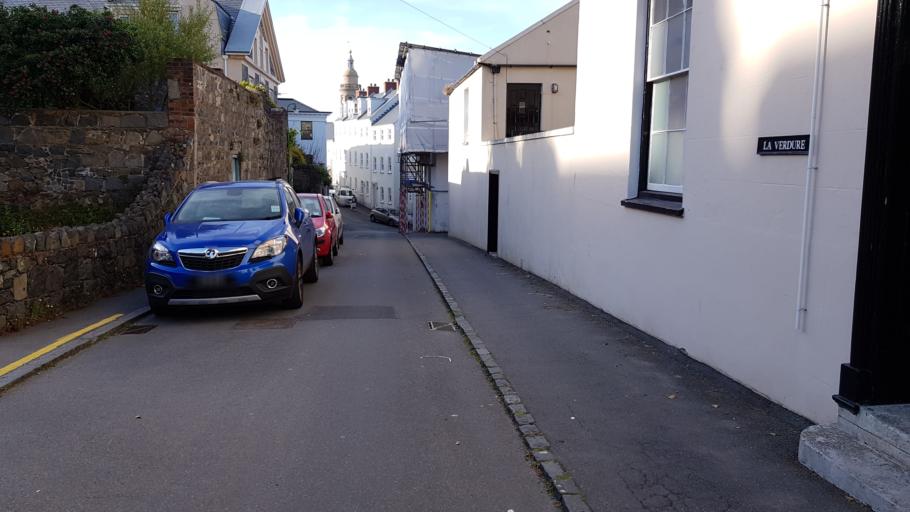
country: GG
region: St Peter Port
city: Saint Peter Port
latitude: 49.4552
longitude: -2.5386
